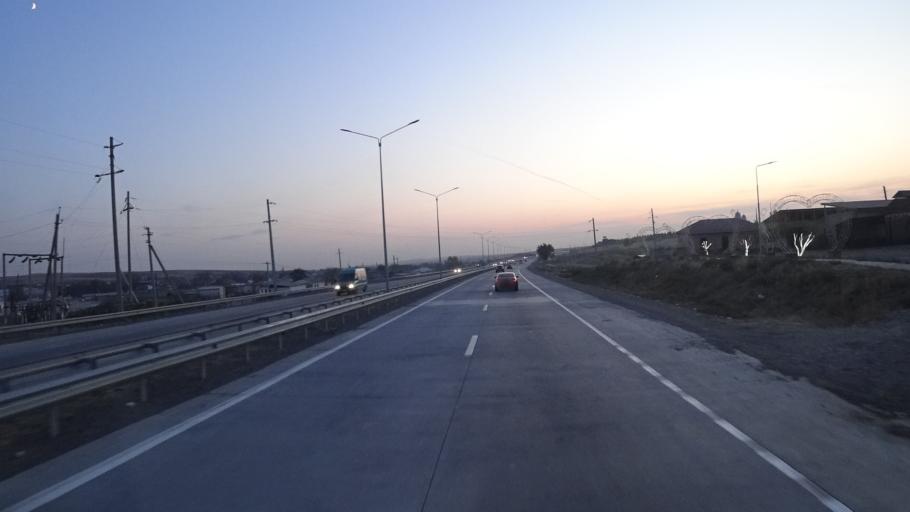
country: KZ
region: Ongtustik Qazaqstan
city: Qazyqurt
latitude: 41.8797
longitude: 69.4355
